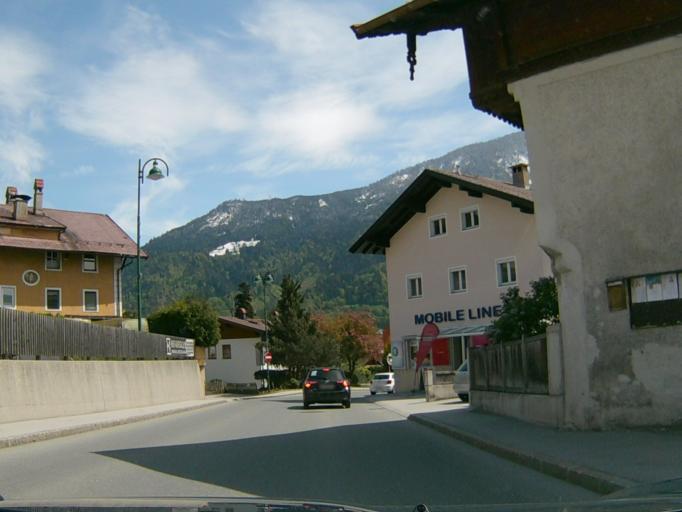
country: AT
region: Tyrol
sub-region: Politischer Bezirk Schwaz
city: Jenbach
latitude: 47.3912
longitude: 11.7717
